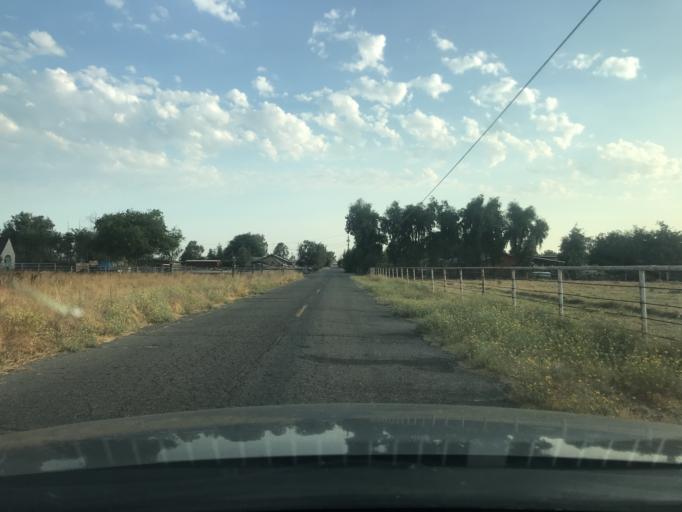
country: US
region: California
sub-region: Merced County
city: Merced
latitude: 37.3639
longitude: -120.4987
